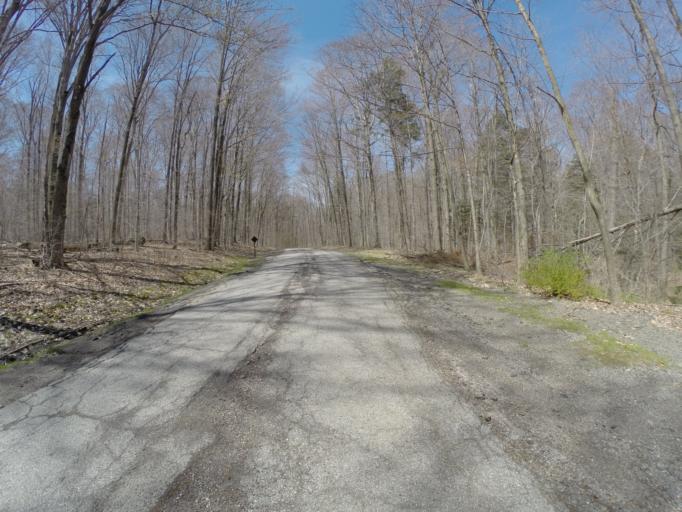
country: US
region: Ohio
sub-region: Cuyahoga County
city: Mayfield
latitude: 41.5523
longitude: -81.4240
